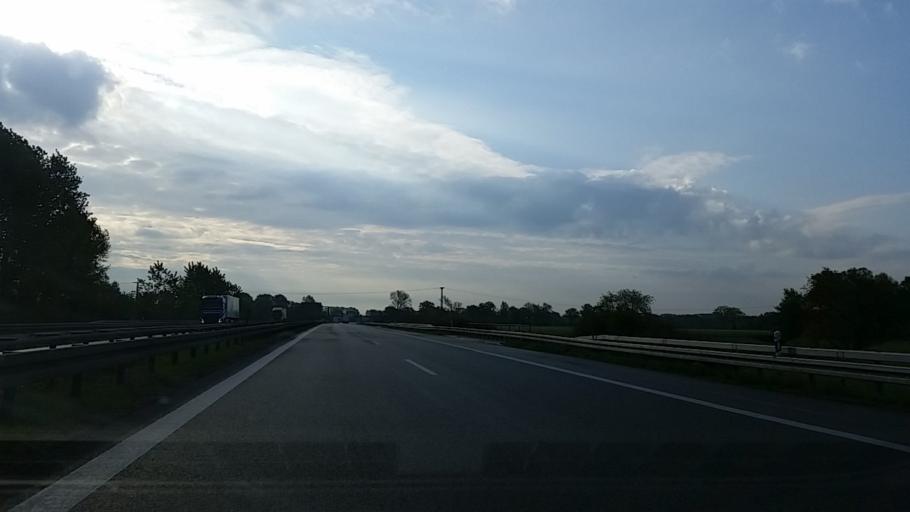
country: DE
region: Mecklenburg-Vorpommern
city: Neustadt-Glewe
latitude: 53.4177
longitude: 11.5410
